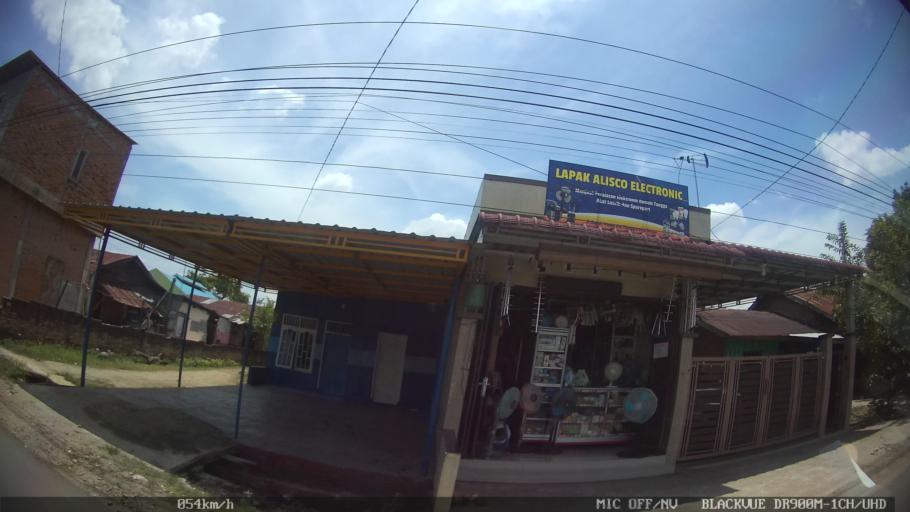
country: ID
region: North Sumatra
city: Binjai
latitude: 3.5971
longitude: 98.5182
